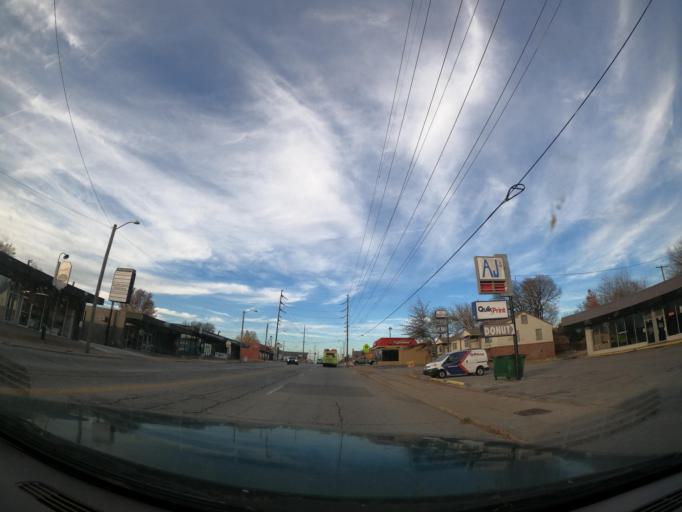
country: US
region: Oklahoma
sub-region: Tulsa County
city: Tulsa
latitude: 36.1345
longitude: -95.9403
